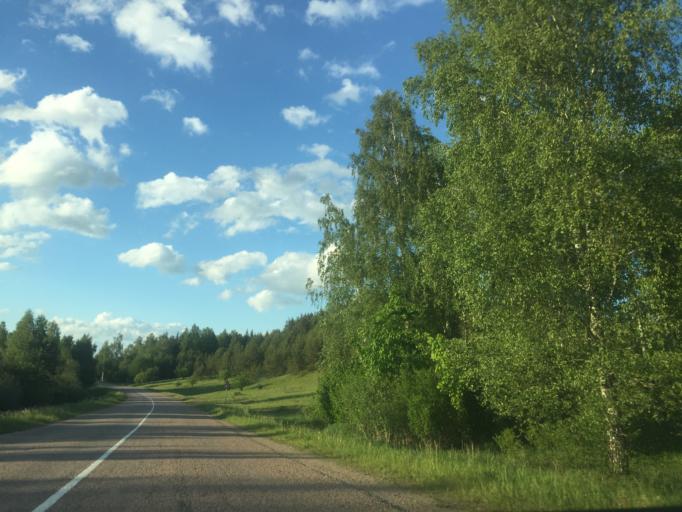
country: LV
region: Kandava
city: Kandava
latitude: 57.0199
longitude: 22.7935
